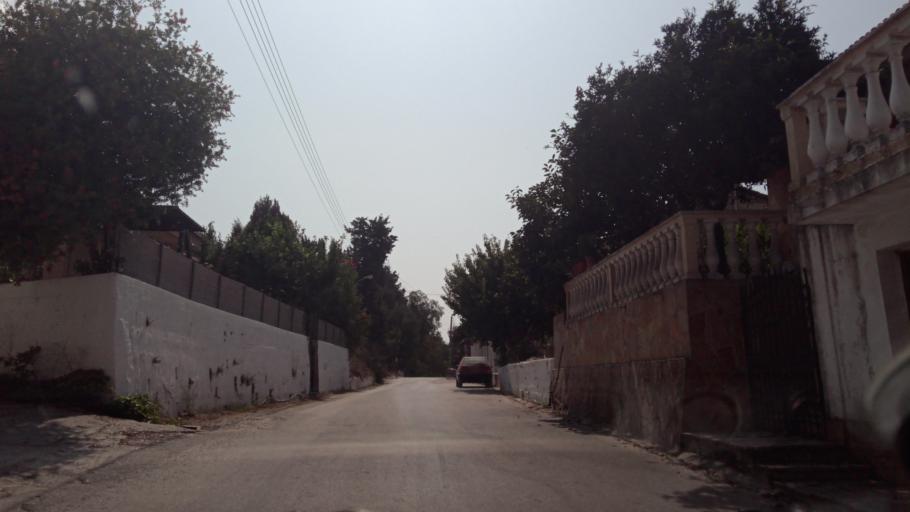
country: GR
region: Ionian Islands
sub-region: Nomos Kerkyras
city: Perivoli
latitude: 39.4100
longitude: 20.0229
